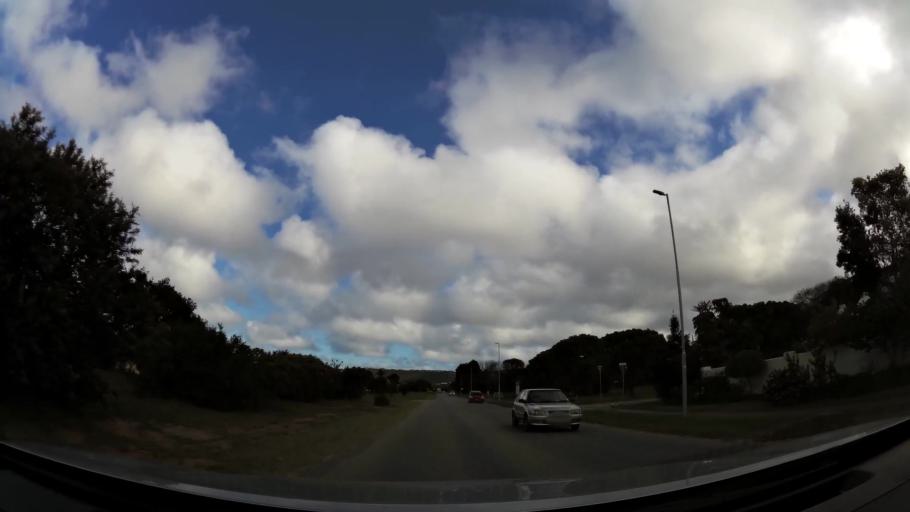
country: ZA
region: Western Cape
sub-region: Eden District Municipality
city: Plettenberg Bay
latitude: -34.0716
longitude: 23.3680
